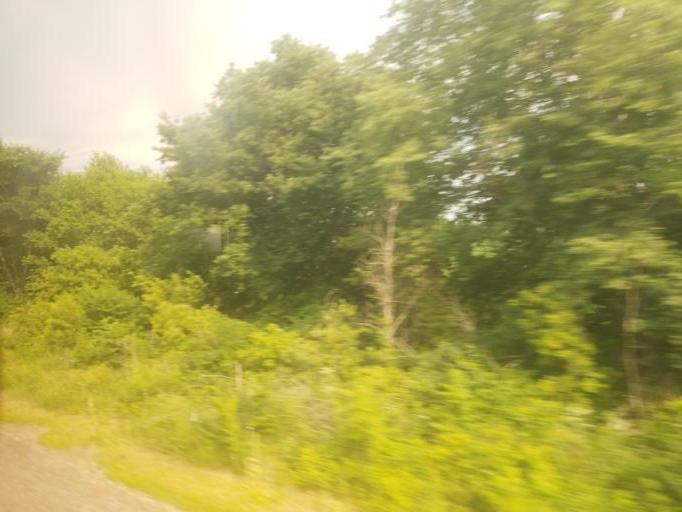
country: US
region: Illinois
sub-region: Bureau County
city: Princeton
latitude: 41.3354
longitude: -89.6667
